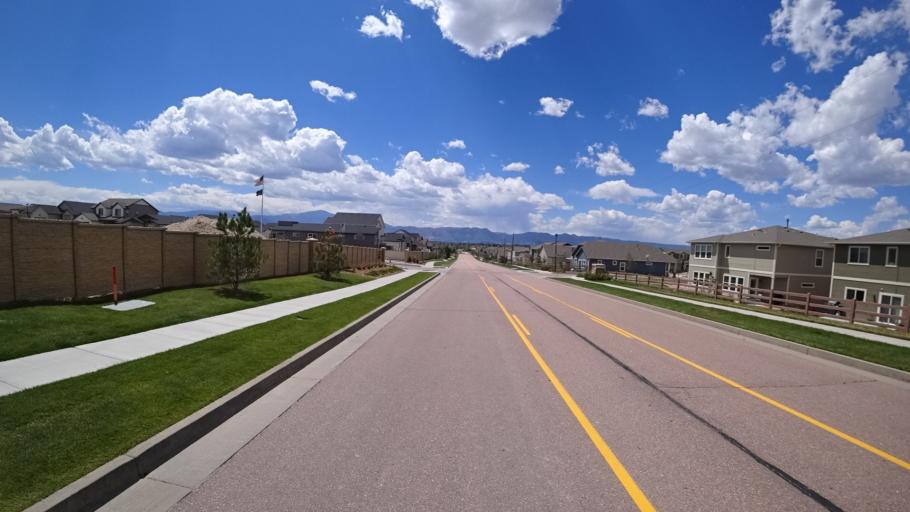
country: US
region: Colorado
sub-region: El Paso County
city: Black Forest
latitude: 38.9514
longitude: -104.7064
